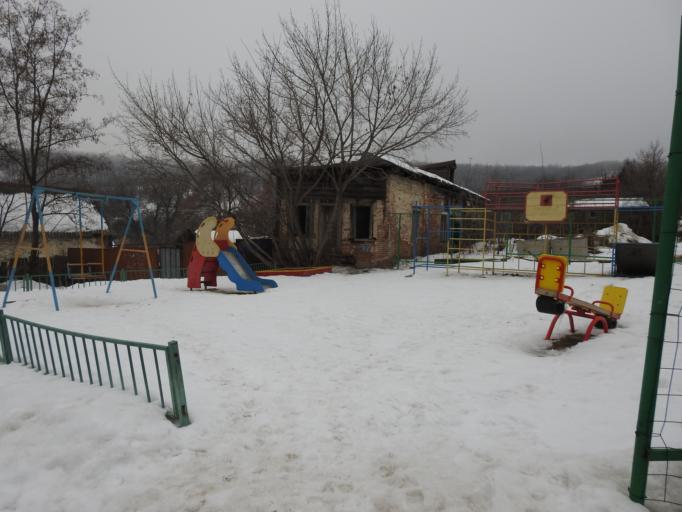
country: RU
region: Saratov
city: Sokolovyy
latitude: 51.4910
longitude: 45.8886
